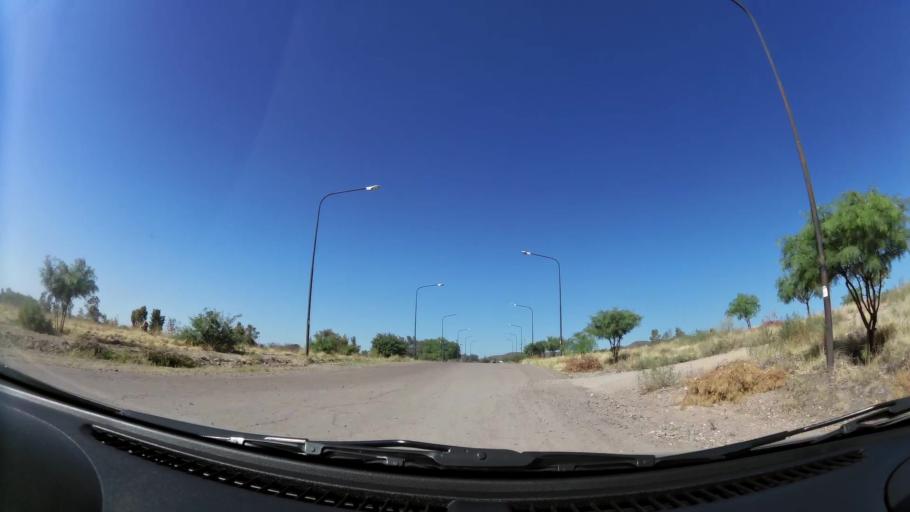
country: AR
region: Mendoza
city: Mendoza
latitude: -32.8960
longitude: -68.8824
